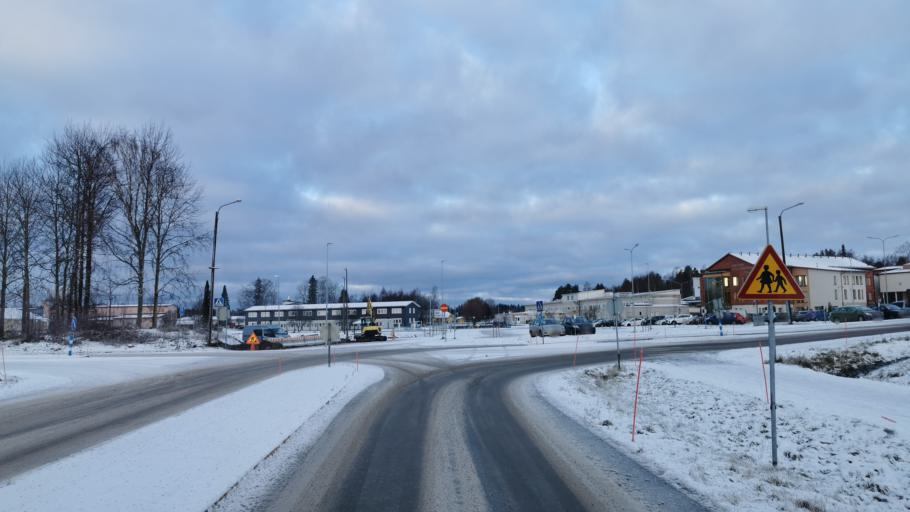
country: FI
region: Ostrobothnia
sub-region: Vaasa
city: Korsholm
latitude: 63.1154
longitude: 21.6856
